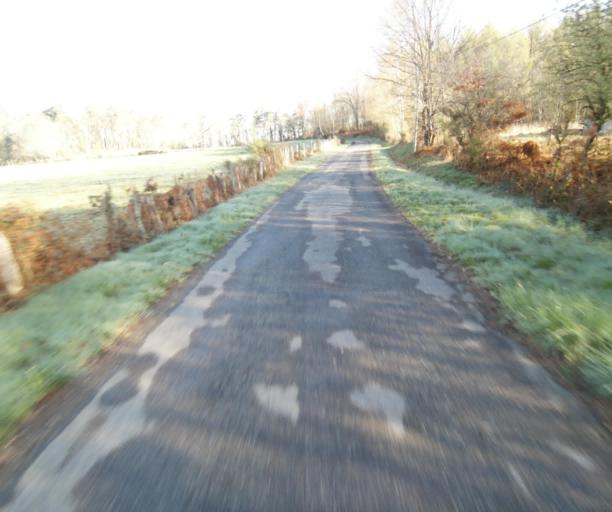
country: FR
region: Limousin
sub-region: Departement de la Correze
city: Correze
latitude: 45.2879
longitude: 1.8638
